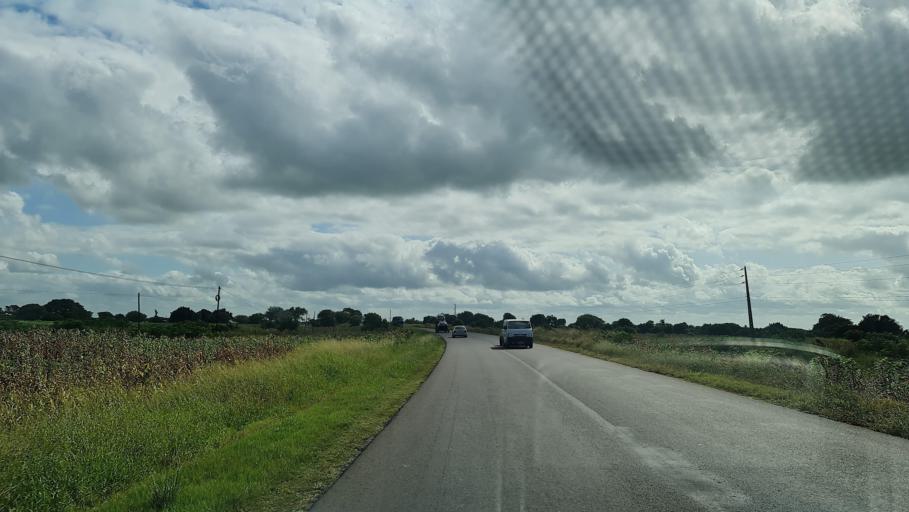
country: MZ
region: Gaza
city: Macia
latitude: -25.0893
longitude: 32.8421
